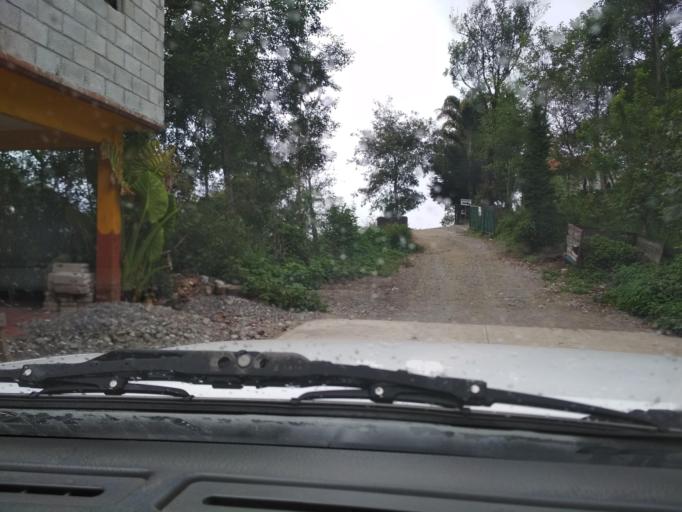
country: MX
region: Veracruz
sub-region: La Perla
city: Chilapa
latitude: 18.9886
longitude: -97.1451
